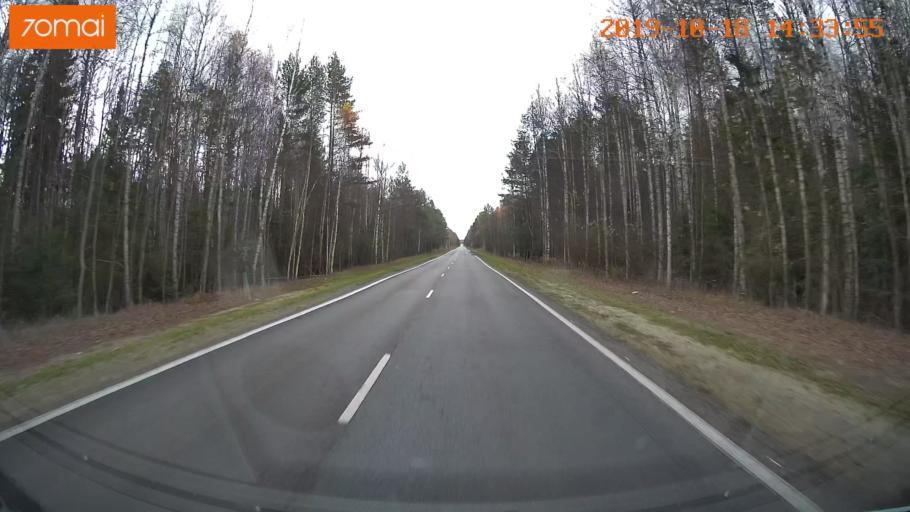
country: RU
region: Vladimir
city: Velikodvorskiy
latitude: 55.2066
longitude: 40.6060
